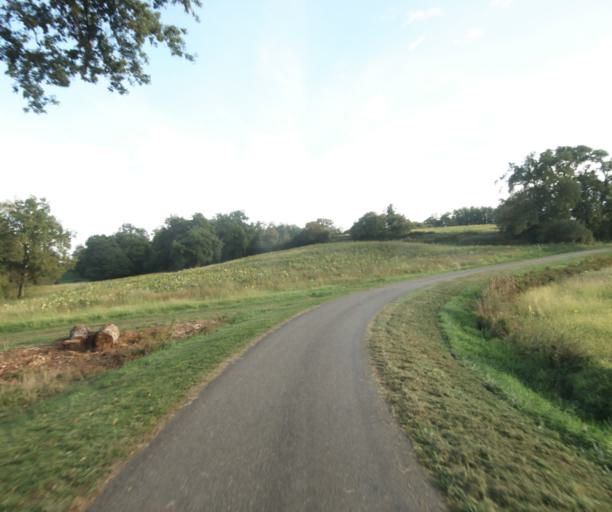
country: FR
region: Midi-Pyrenees
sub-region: Departement du Gers
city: Le Houga
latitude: 43.8452
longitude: -0.1235
